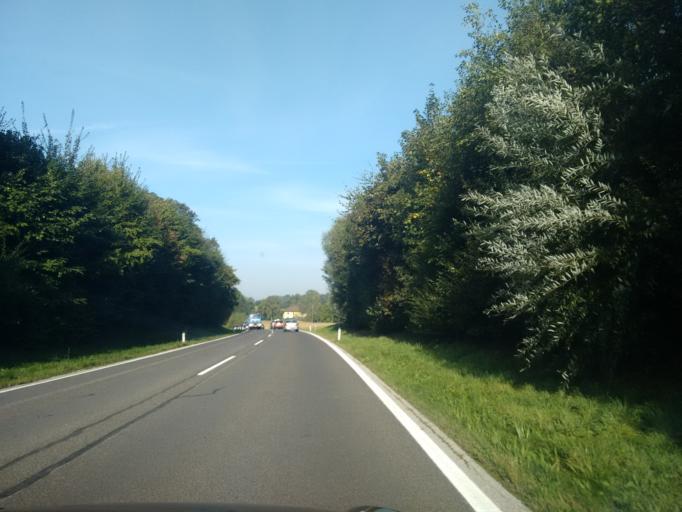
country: AT
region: Upper Austria
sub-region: Politischer Bezirk Grieskirchen
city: Grieskirchen
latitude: 48.2774
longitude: 13.7285
